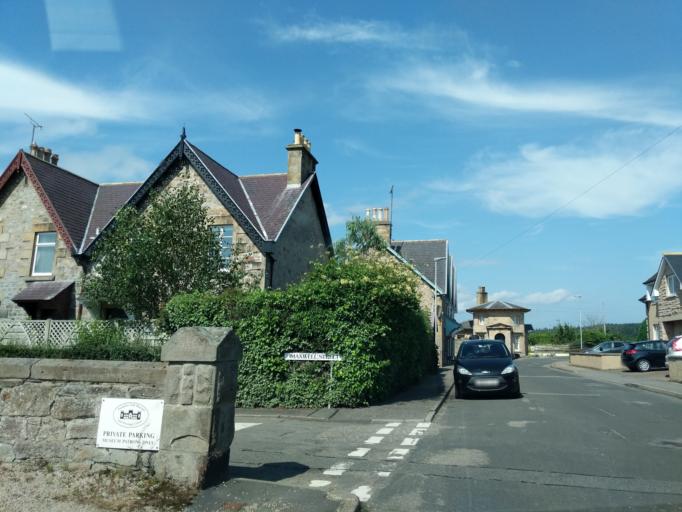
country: GB
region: Scotland
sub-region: Moray
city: Fochabers
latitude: 57.6134
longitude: -3.0932
